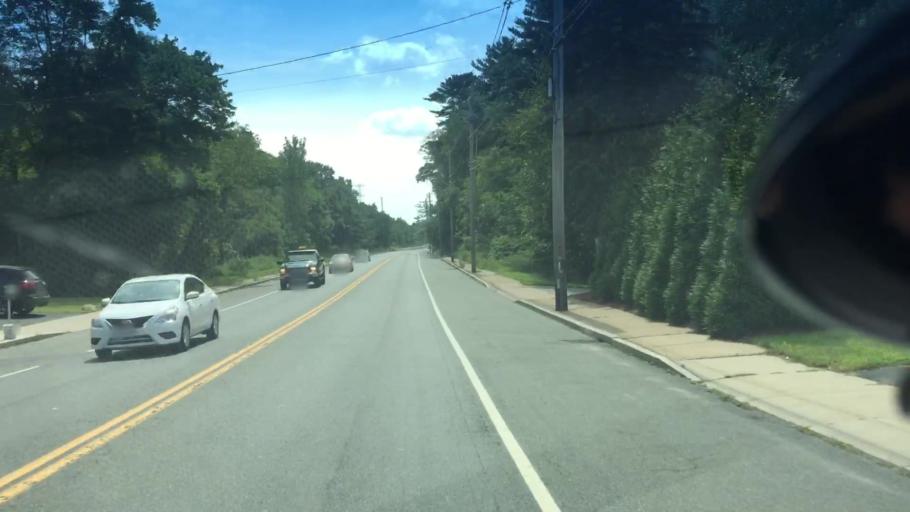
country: US
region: Massachusetts
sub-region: Norfolk County
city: Stoughton
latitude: 42.1481
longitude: -71.0750
